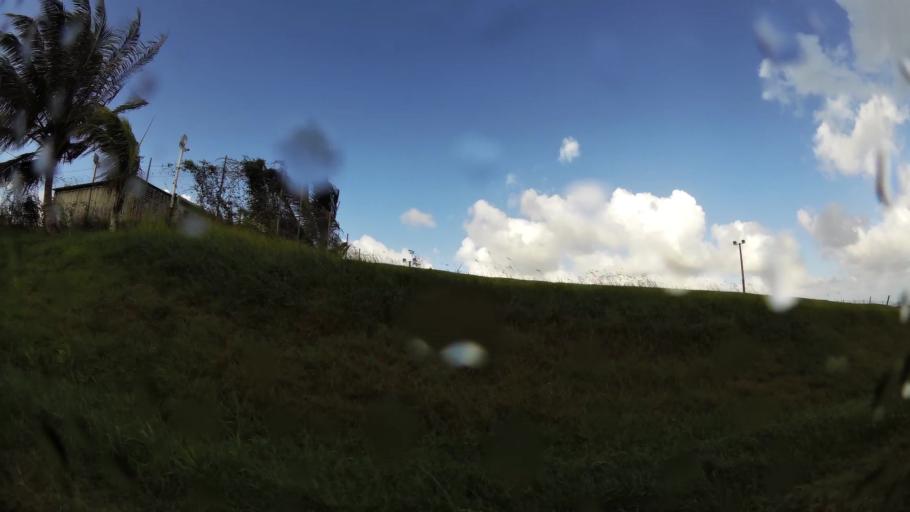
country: MQ
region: Martinique
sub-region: Martinique
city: Les Trois-Ilets
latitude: 14.5362
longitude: -61.0377
